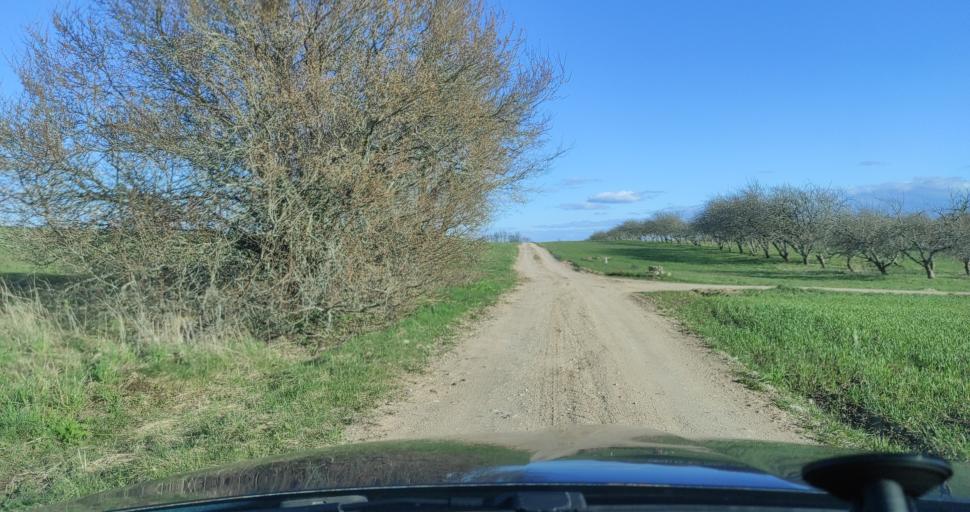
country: LV
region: Kuldigas Rajons
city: Kuldiga
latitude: 56.8722
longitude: 21.8386
